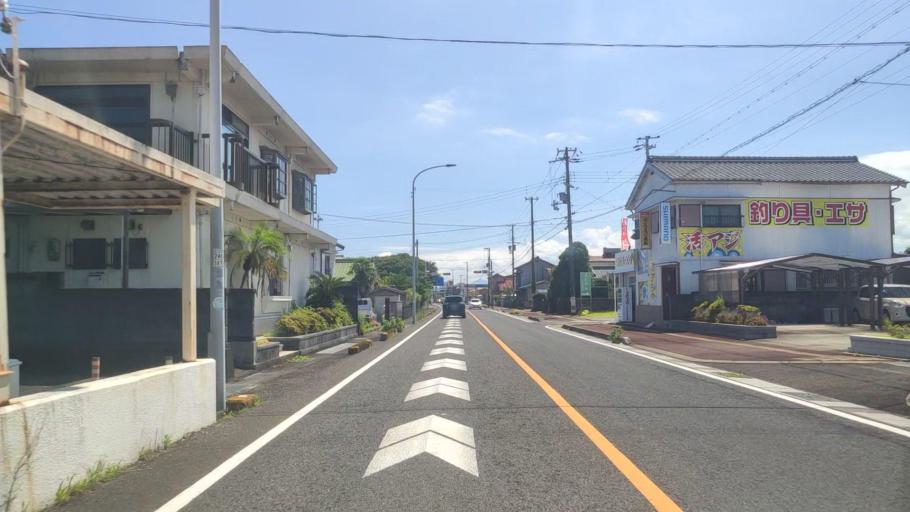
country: JP
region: Wakayama
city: Shingu
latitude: 33.8729
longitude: 136.0864
